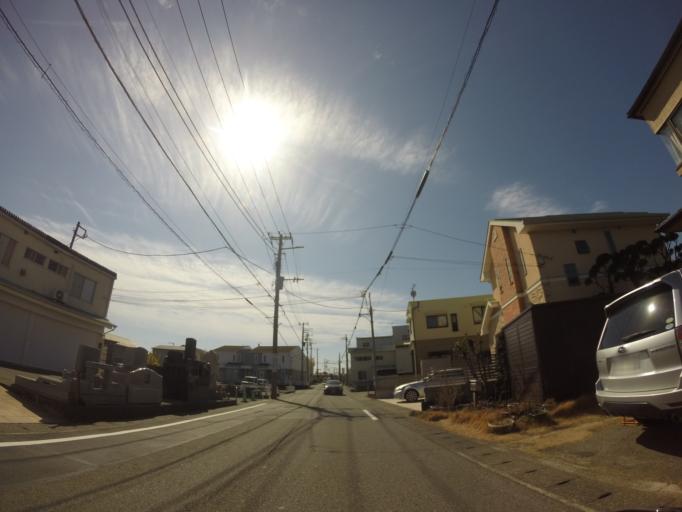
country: JP
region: Shizuoka
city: Numazu
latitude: 35.1184
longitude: 138.8209
